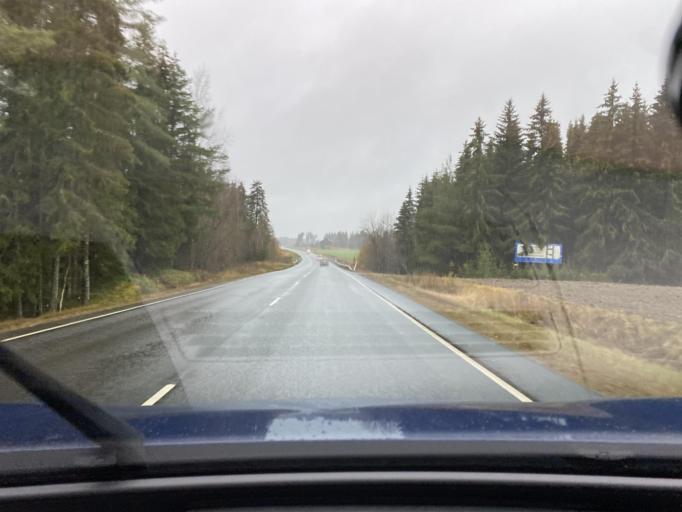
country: FI
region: Varsinais-Suomi
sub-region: Loimaa
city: Alastaro
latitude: 60.9316
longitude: 22.8743
